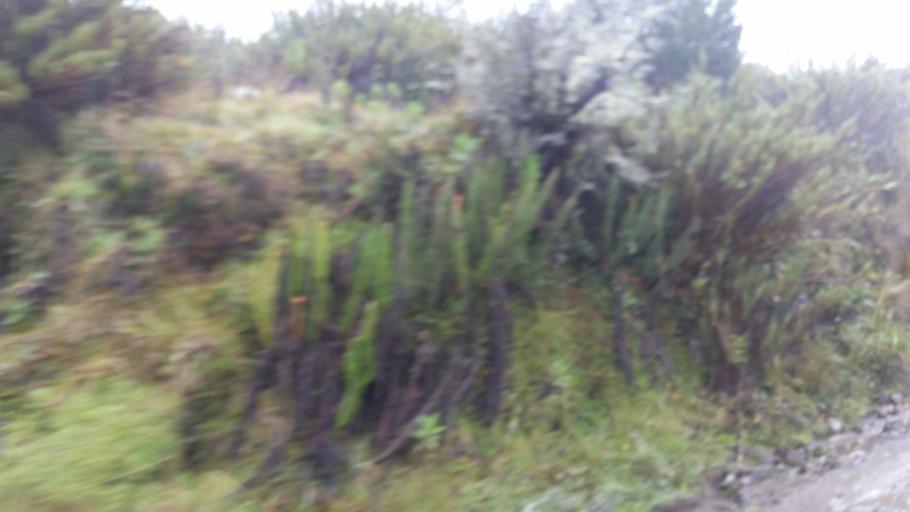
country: CO
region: Cundinamarca
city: La Calera
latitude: 4.6899
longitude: -73.8011
